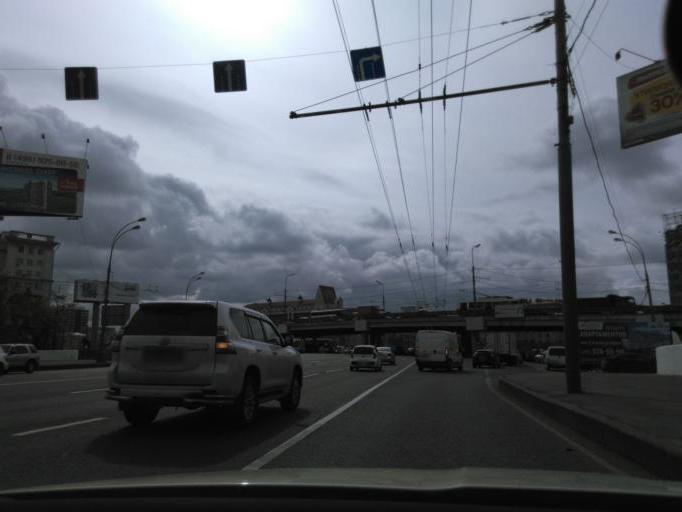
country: RU
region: Moscow
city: Mar'ina Roshcha
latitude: 55.7930
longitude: 37.5869
